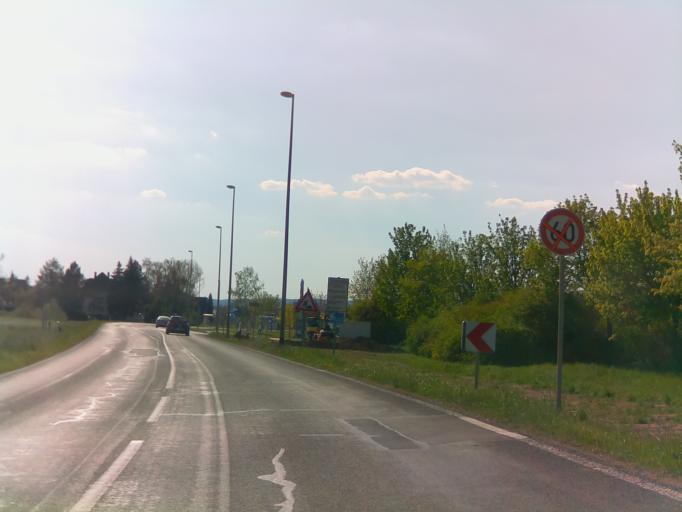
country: DE
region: Thuringia
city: Dreitzsch
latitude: 50.7390
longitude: 11.7760
